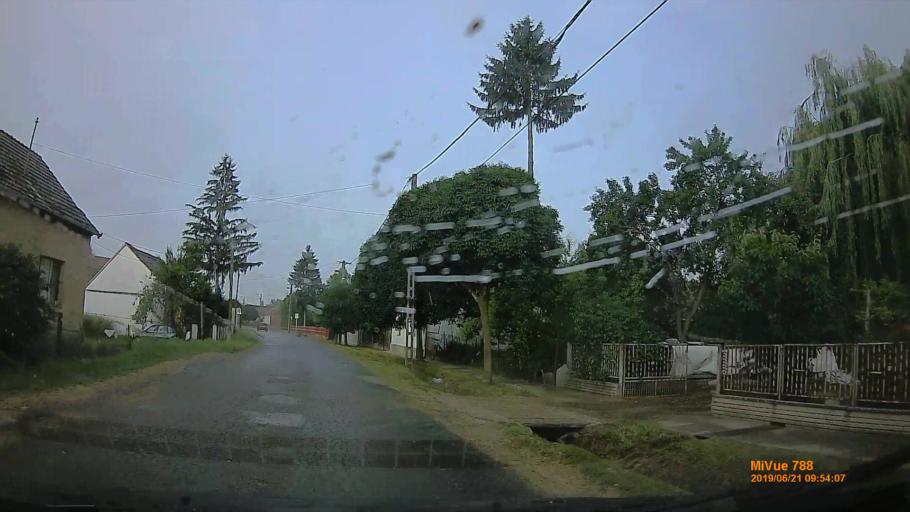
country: HU
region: Baranya
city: Sasd
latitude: 46.2331
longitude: 17.9991
